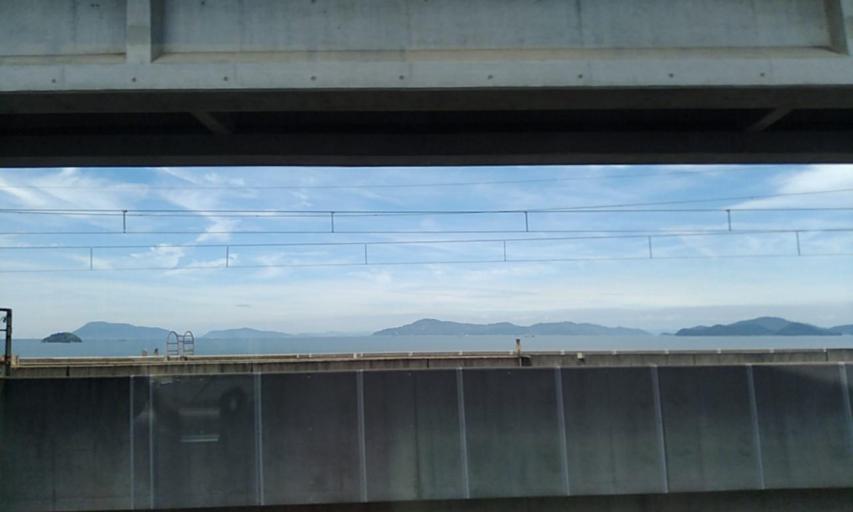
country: JP
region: Kagawa
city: Sakaidecho
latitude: 34.3195
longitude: 133.8224
